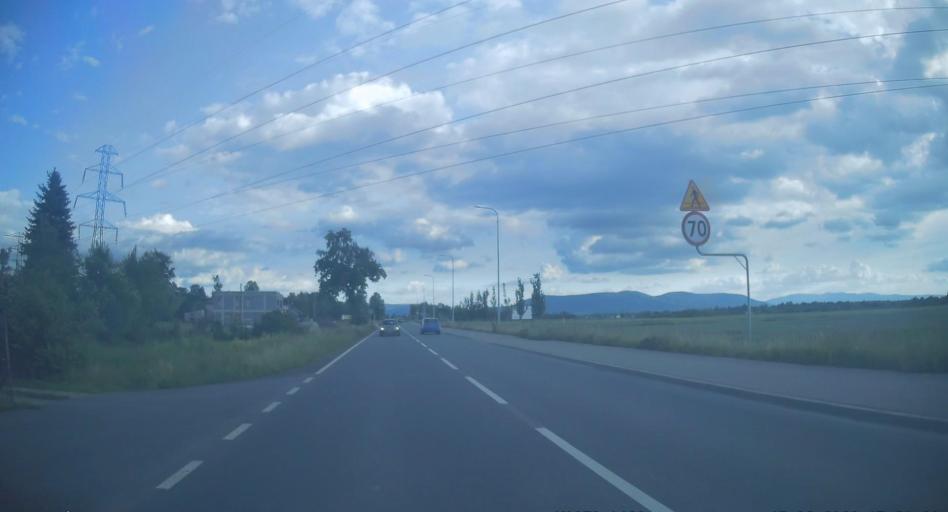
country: PL
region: Lesser Poland Voivodeship
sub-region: Powiat oswiecimski
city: Nowa Wies
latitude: 49.9243
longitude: 19.2136
